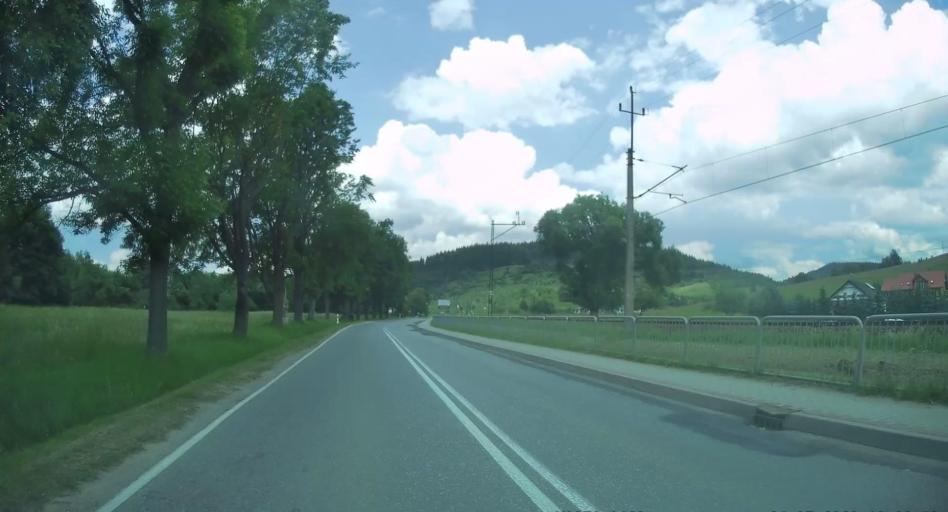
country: PL
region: Lesser Poland Voivodeship
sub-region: Powiat nowosadecki
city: Krynica-Zdroj
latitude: 49.3784
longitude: 20.9509
